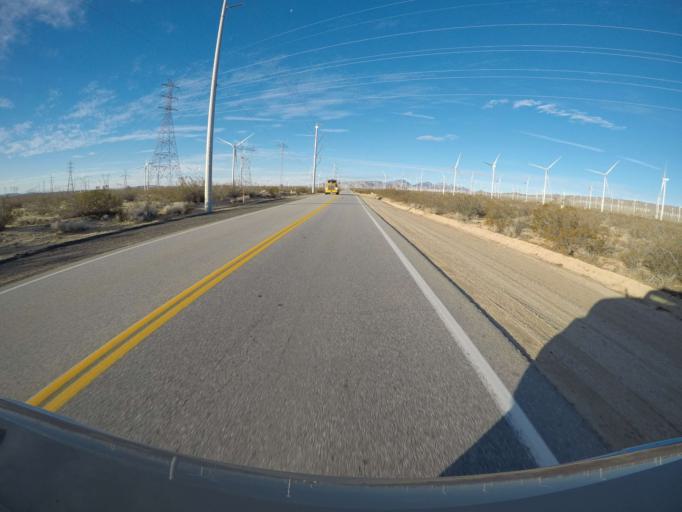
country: US
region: California
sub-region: Kern County
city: Mojave
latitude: 35.0491
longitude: -118.2079
